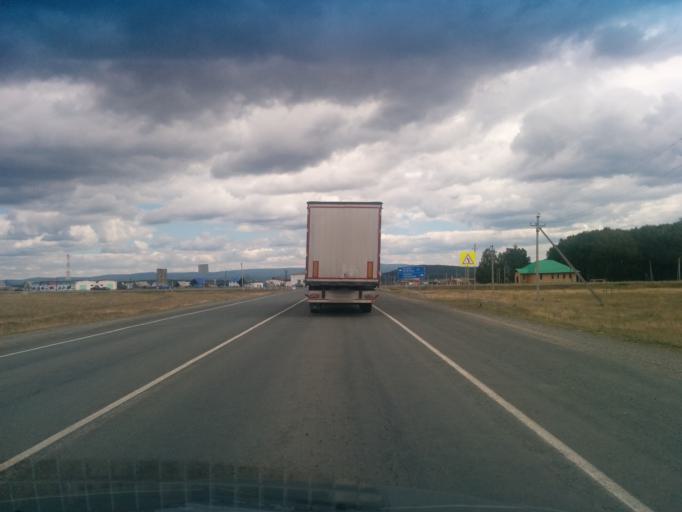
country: RU
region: Bashkortostan
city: Lomovka
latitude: 53.8809
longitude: 58.1062
